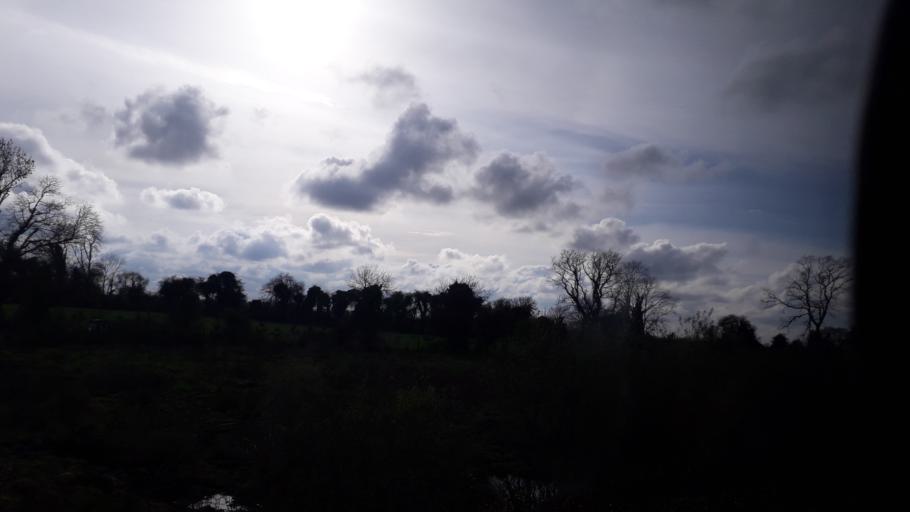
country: IE
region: Leinster
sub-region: An Mhi
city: Longwood
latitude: 53.4417
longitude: -6.9309
